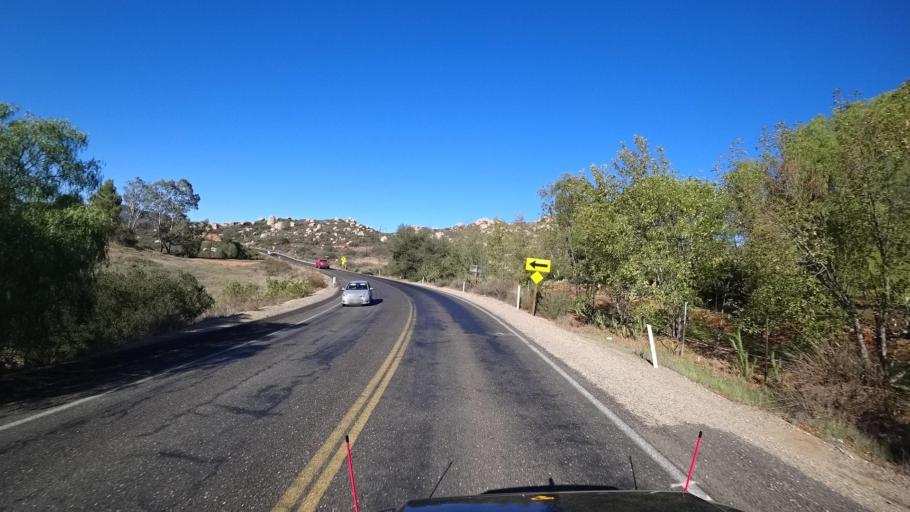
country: MX
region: Baja California
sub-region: Tijuana
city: Villa del Campo
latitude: 32.6243
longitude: -116.7527
